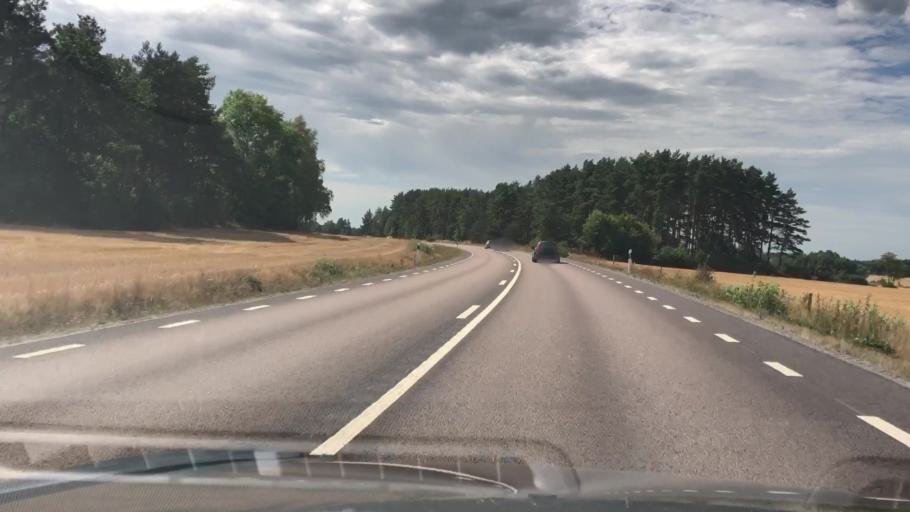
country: SE
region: Kalmar
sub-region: Torsas Kommun
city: Torsas
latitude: 56.3521
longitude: 16.0511
